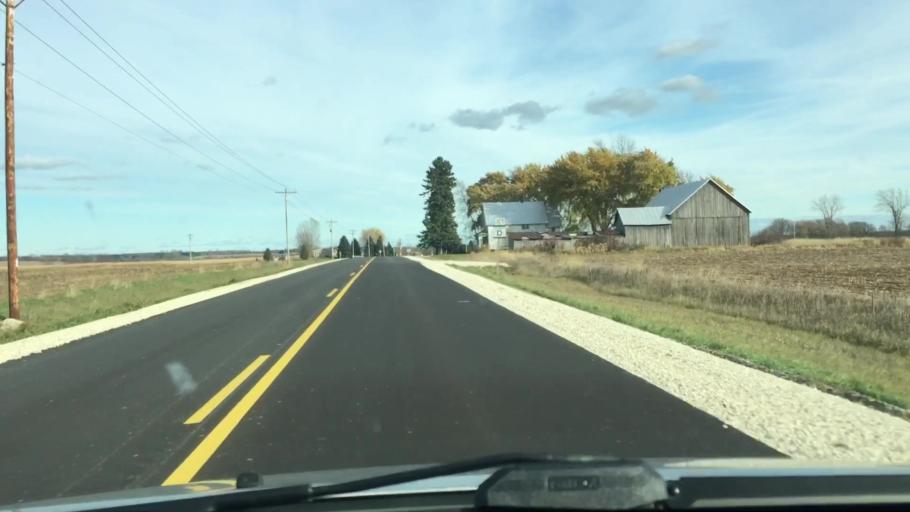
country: US
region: Wisconsin
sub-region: Kewaunee County
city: Algoma
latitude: 44.6899
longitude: -87.5134
